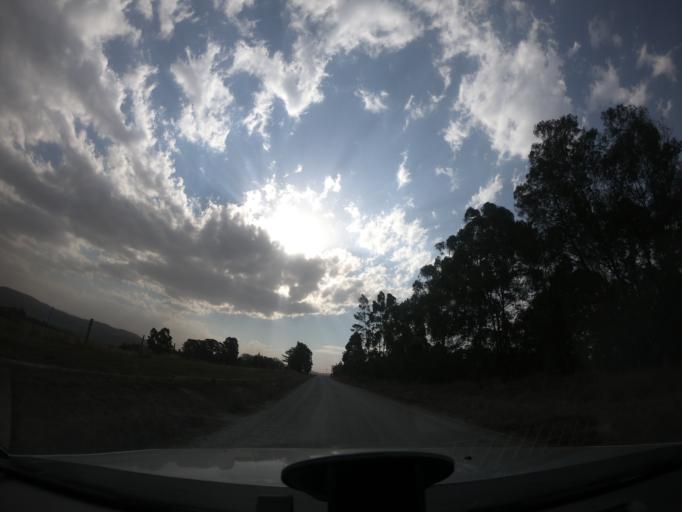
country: ZA
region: KwaZulu-Natal
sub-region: uMgungundlovu District Municipality
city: Howick
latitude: -29.4283
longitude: 30.1081
